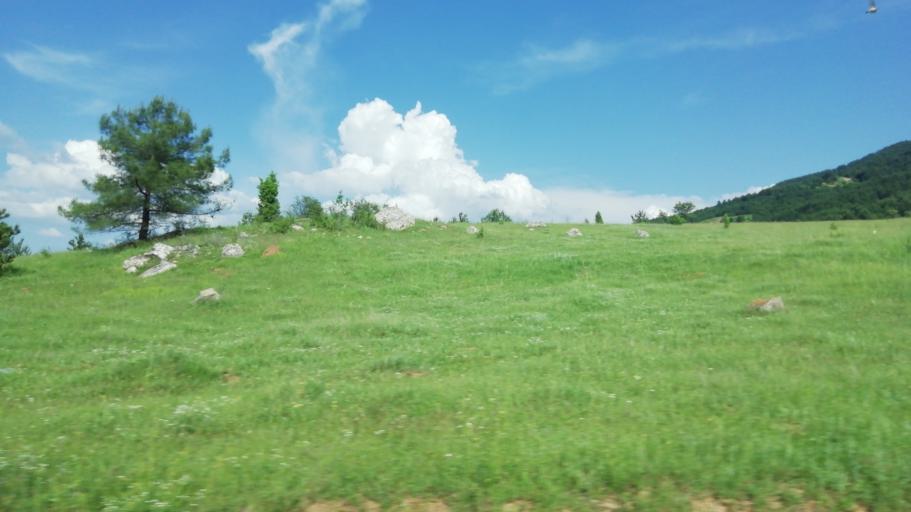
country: TR
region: Karabuk
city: Karabuk
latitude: 41.1294
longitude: 32.5762
